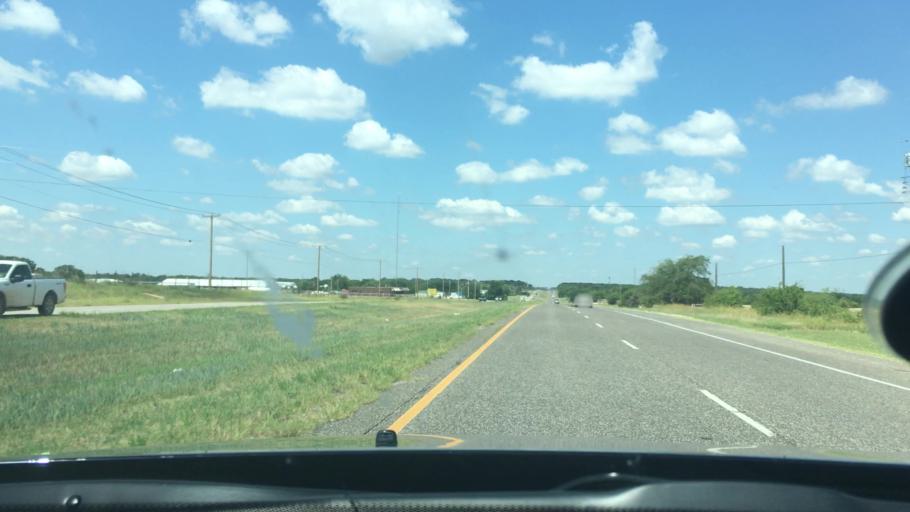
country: US
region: Oklahoma
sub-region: Carter County
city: Lone Grove
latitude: 34.1731
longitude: -97.2742
